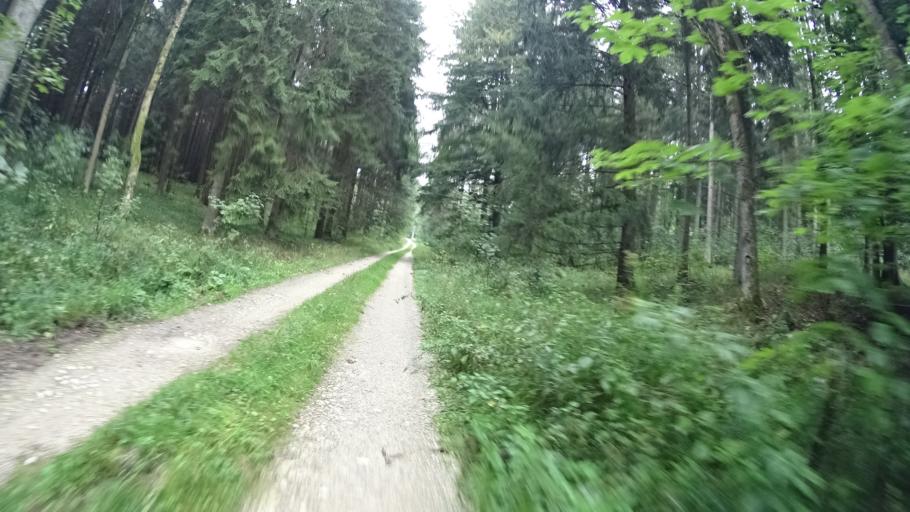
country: DE
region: Bavaria
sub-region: Upper Bavaria
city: Denkendorf
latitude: 48.8970
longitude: 11.4590
